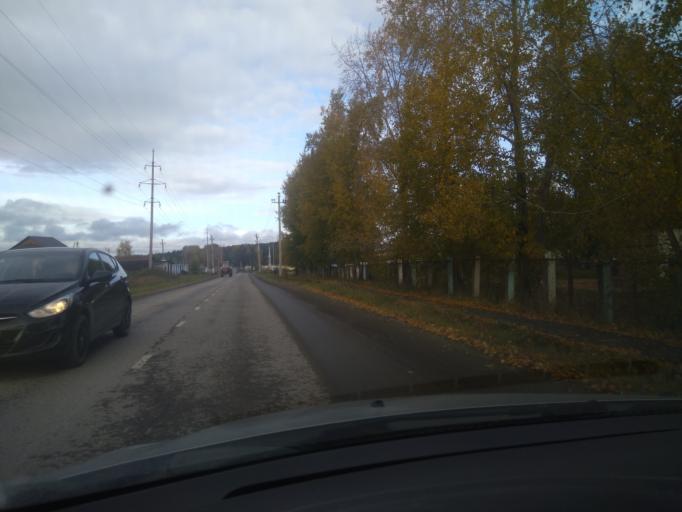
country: RU
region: Sverdlovsk
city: Nikolo-Pavlovskoye
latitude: 57.7976
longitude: 60.0507
